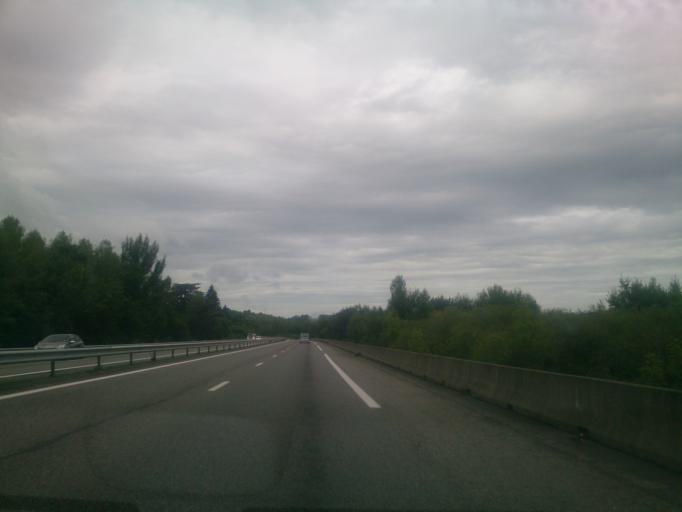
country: FR
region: Midi-Pyrenees
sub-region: Departement de la Haute-Garonne
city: Montrejeau
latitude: 43.0969
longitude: 0.5677
